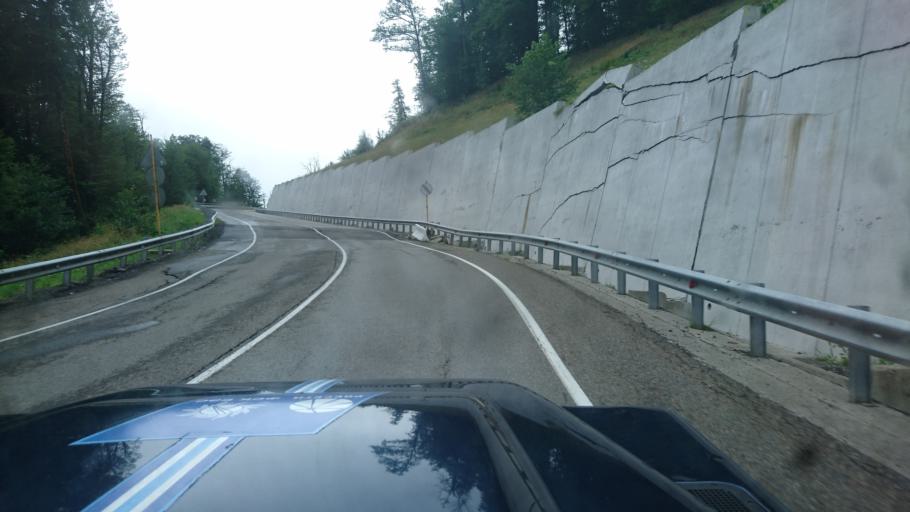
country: RU
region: Krasnodarskiy
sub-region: Sochi City
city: Krasnaya Polyana
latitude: 43.6614
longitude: 40.3107
